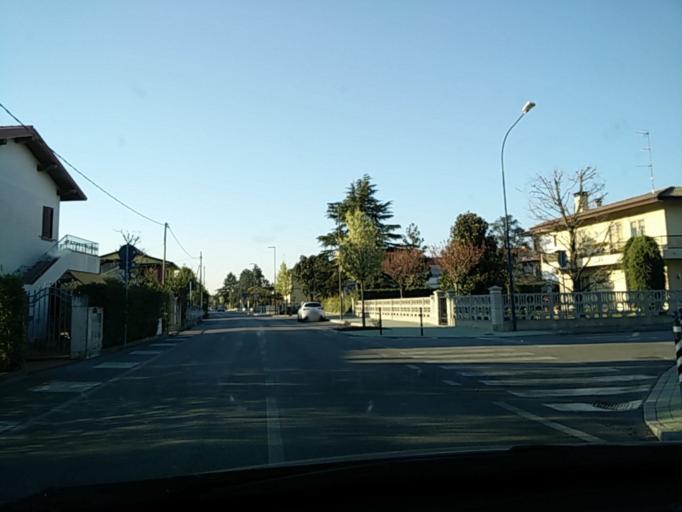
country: IT
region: Veneto
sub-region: Provincia di Venezia
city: San Dona di Piave
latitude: 45.6169
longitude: 12.5684
